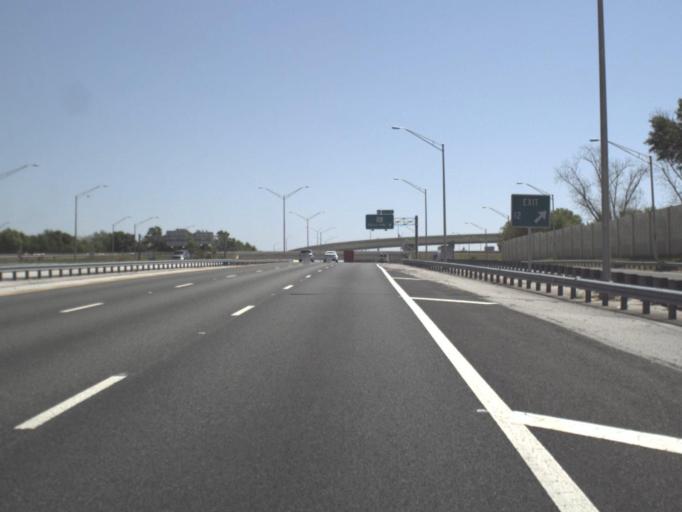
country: US
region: Florida
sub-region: Escambia County
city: Ferry Pass
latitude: 30.5034
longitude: -87.2352
